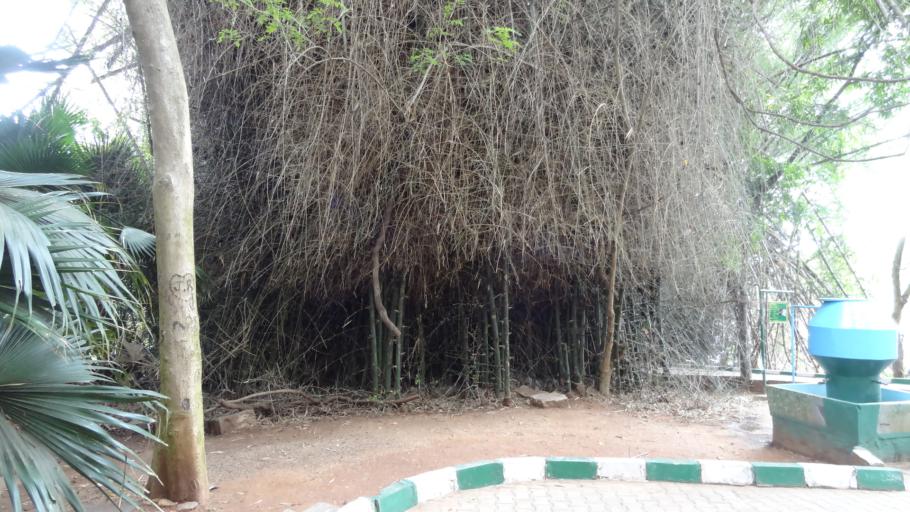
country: IN
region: Karnataka
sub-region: Mandya
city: Shrirangapattana
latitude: 12.4244
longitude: 76.6563
